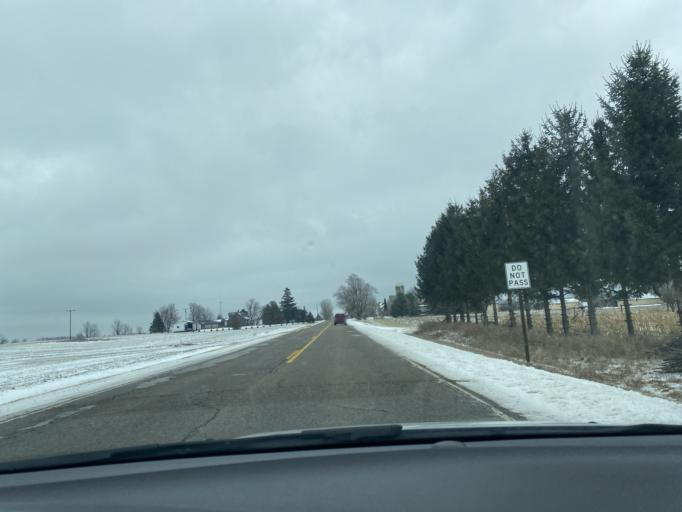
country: US
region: Michigan
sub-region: Sanilac County
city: Brown City
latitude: 43.2103
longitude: -83.0931
